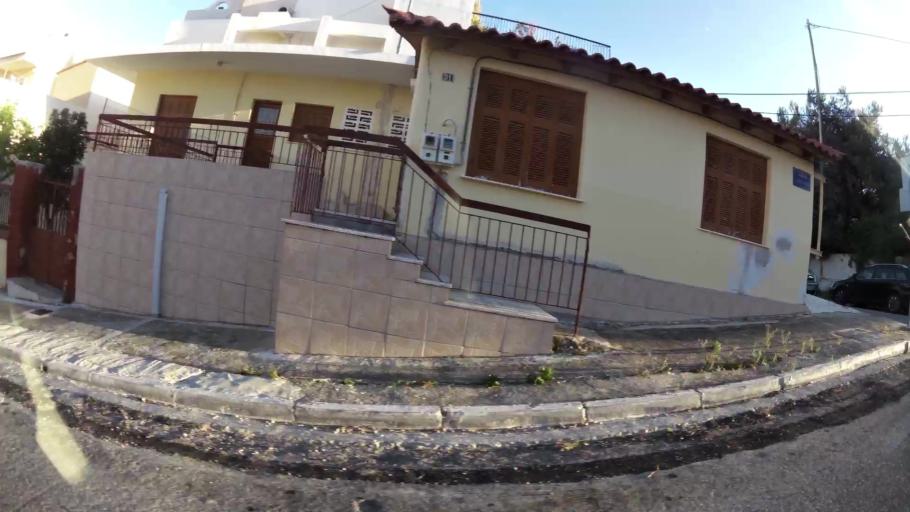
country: GR
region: Attica
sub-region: Nomarchia Anatolikis Attikis
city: Rafina
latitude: 38.0211
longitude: 24.0054
